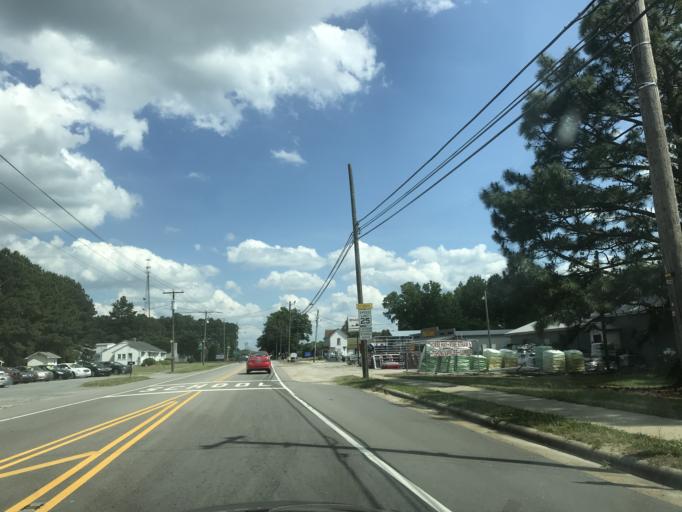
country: US
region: North Carolina
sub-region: Nash County
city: Spring Hope
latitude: 35.9578
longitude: -78.2506
